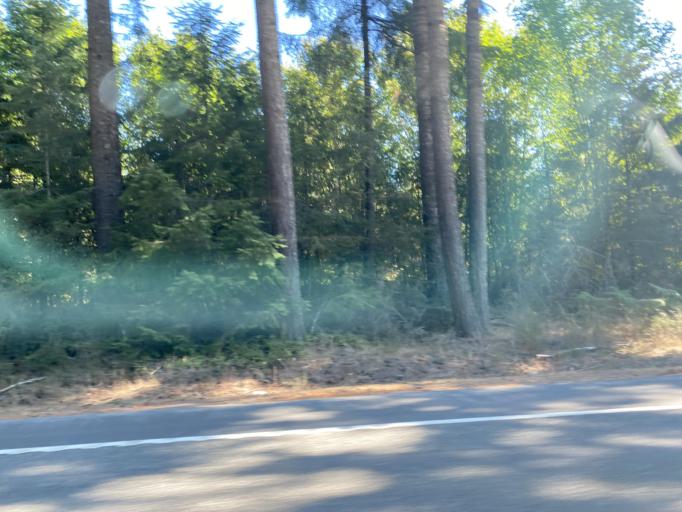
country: US
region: Washington
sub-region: Thurston County
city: Rainier
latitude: 46.9198
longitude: -122.7465
